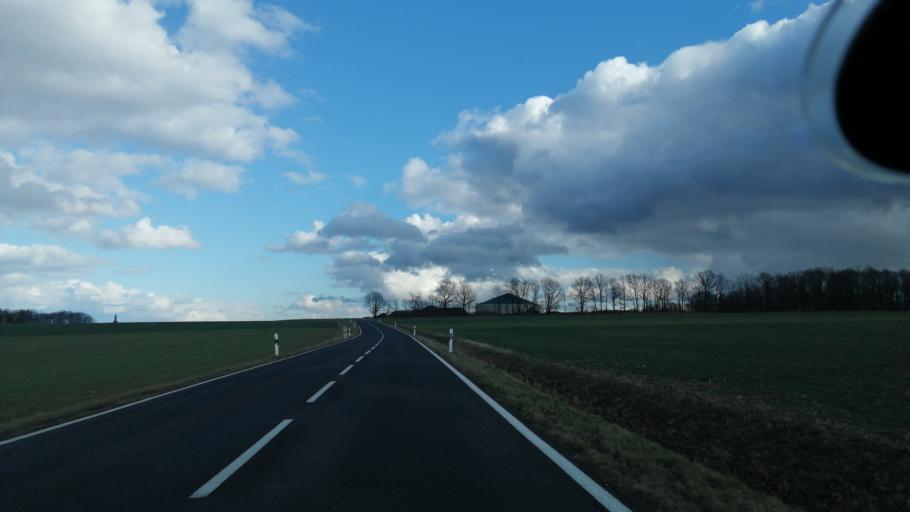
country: DE
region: Saxony
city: Hochkirch
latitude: 51.1443
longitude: 14.5500
